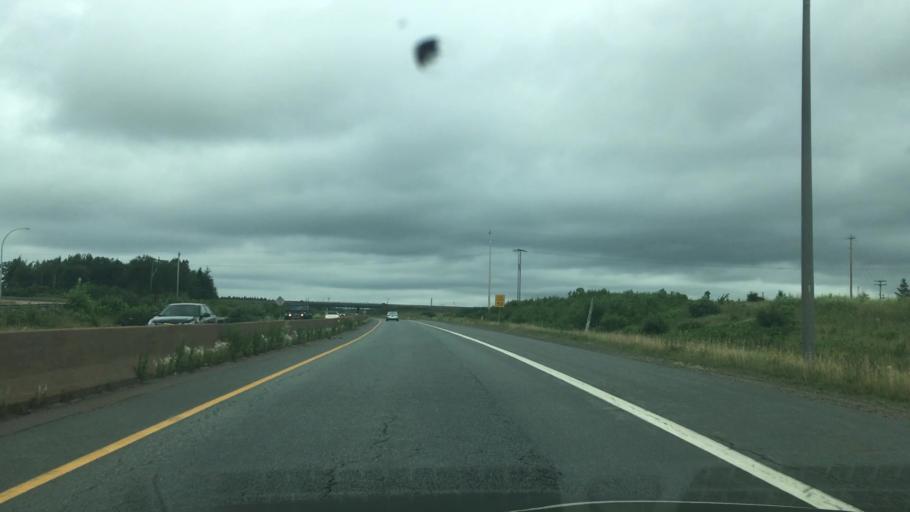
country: CA
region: Nova Scotia
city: Truro
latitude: 45.3860
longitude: -63.3224
